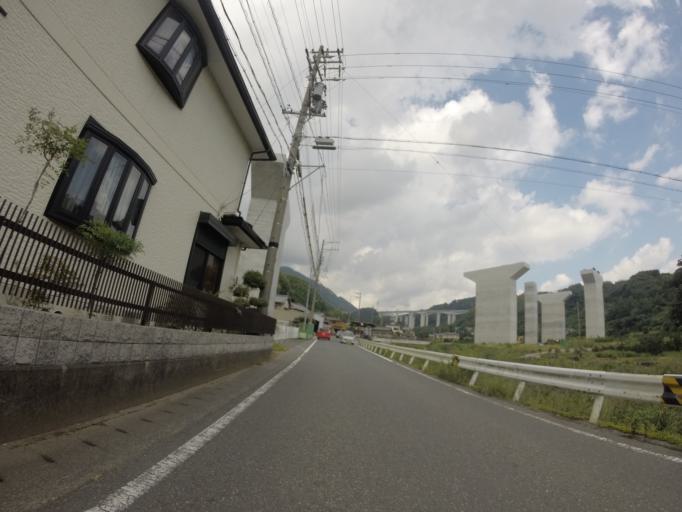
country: JP
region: Shizuoka
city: Shizuoka-shi
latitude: 35.0644
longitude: 138.4703
